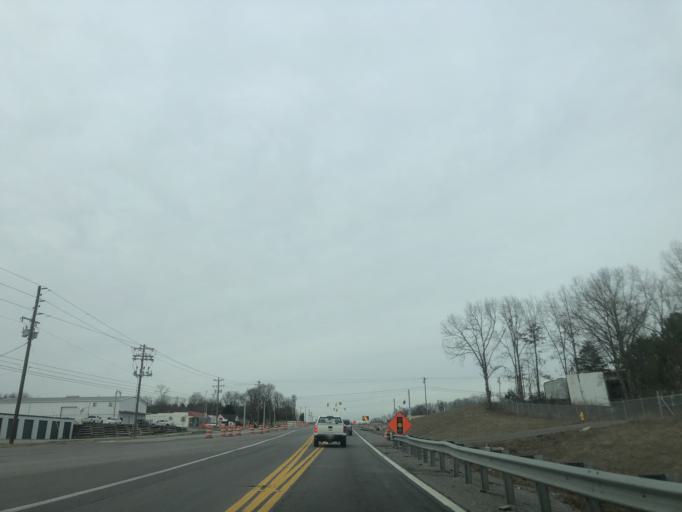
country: US
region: Tennessee
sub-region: Sumner County
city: Gallatin
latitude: 36.2903
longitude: -86.4436
